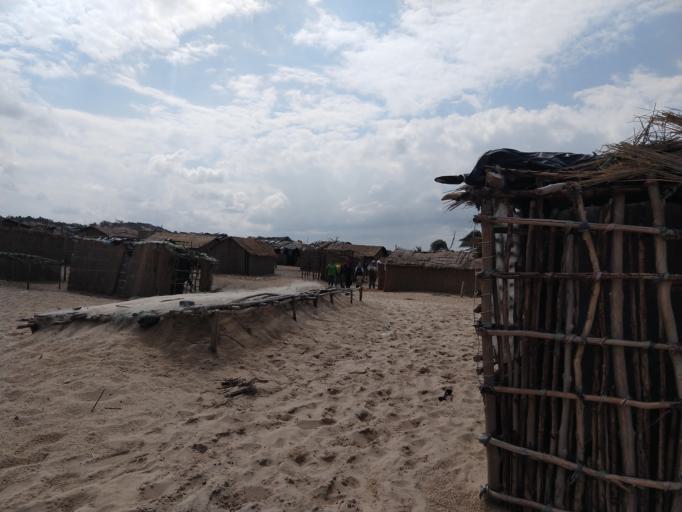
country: MZ
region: Sofala
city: Beira
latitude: -19.6500
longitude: 35.1784
